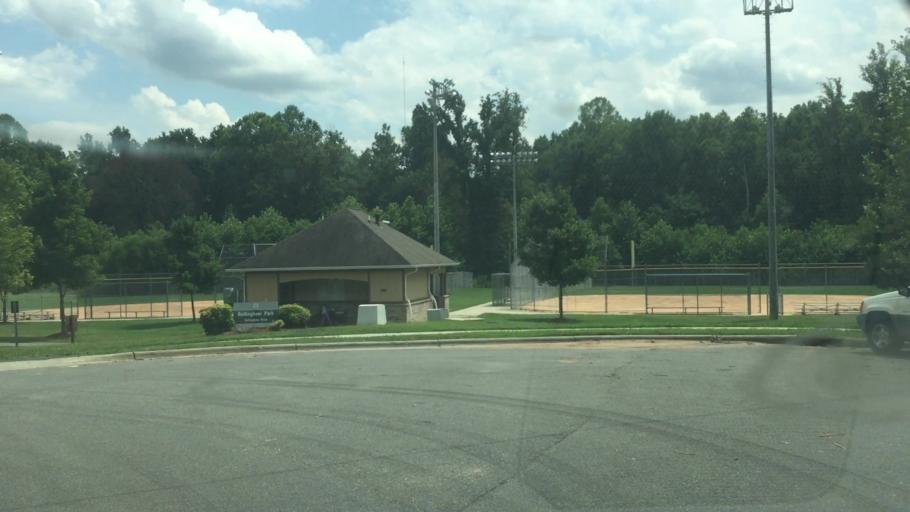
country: US
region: North Carolina
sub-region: Iredell County
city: Mooresville
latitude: 35.5518
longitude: -80.8024
